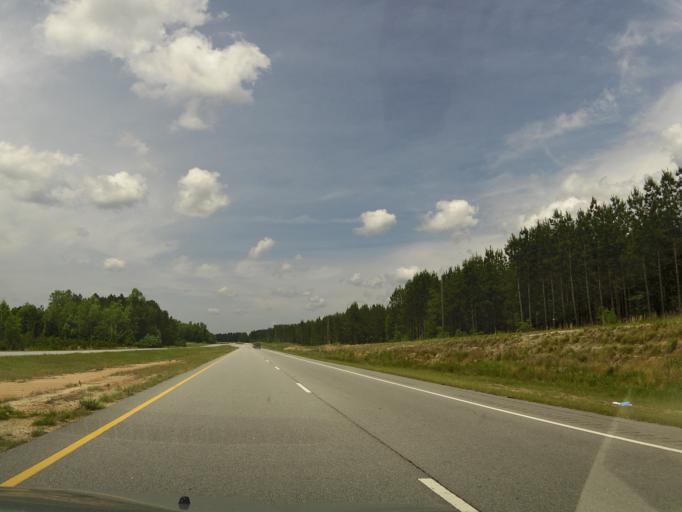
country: US
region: Georgia
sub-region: Jefferson County
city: Wadley
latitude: 32.7621
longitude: -82.3856
